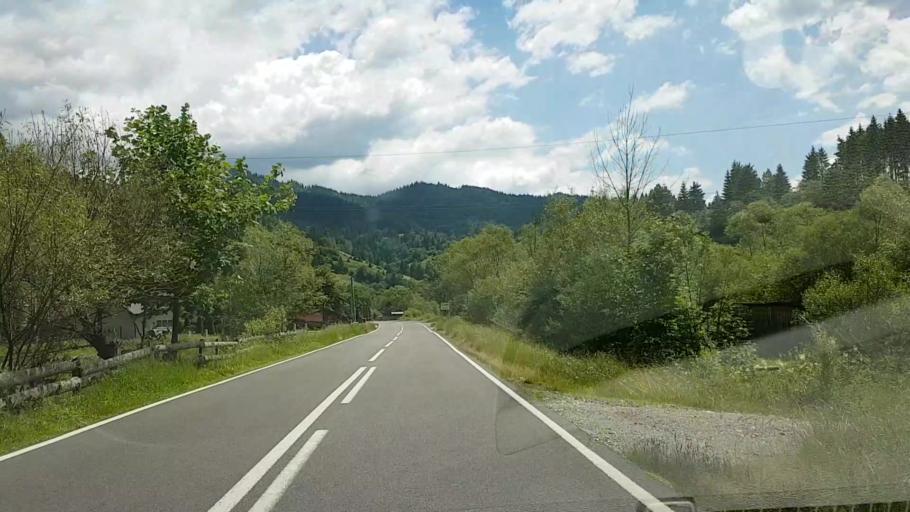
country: RO
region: Suceava
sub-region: Comuna Crucea
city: Crucea
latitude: 47.3929
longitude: 25.5724
